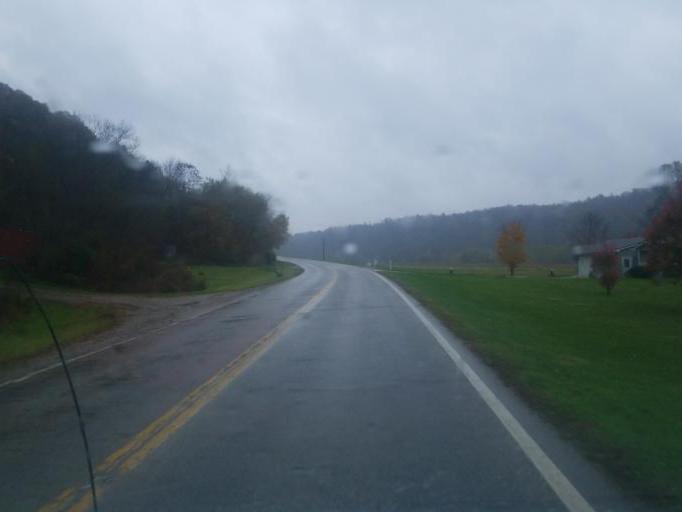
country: US
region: Ohio
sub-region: Morgan County
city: McConnelsville
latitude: 39.6210
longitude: -81.8349
